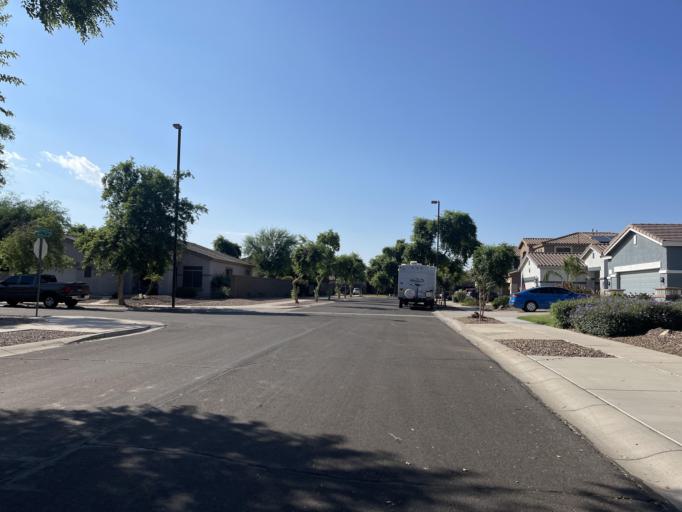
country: US
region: Arizona
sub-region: Maricopa County
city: Queen Creek
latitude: 33.2655
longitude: -111.7029
